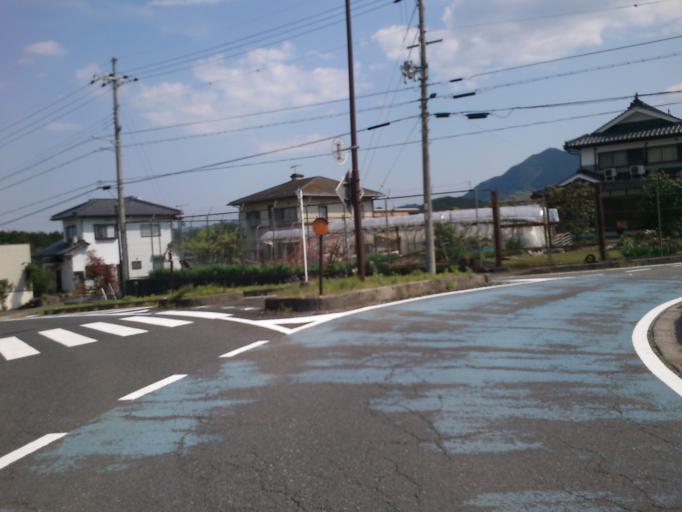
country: JP
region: Kyoto
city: Fukuchiyama
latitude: 35.3382
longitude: 134.9302
